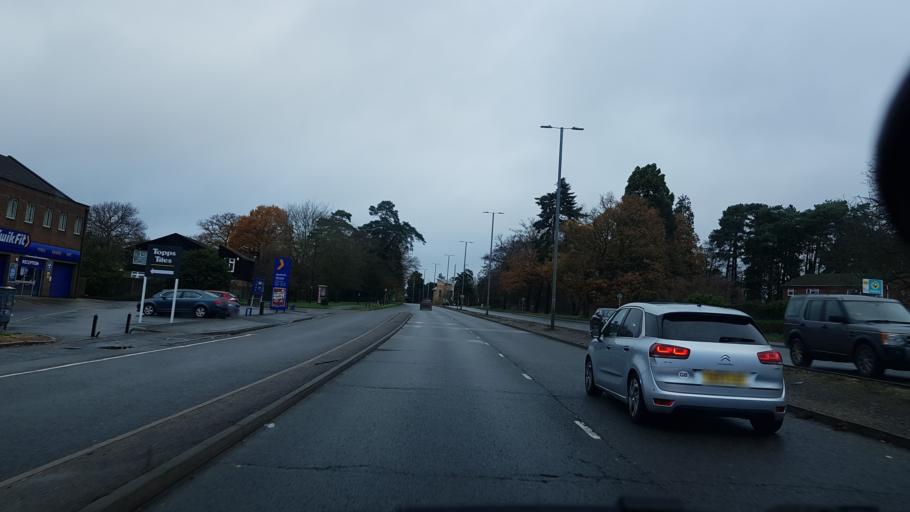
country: GB
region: England
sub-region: Bracknell Forest
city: Bracknell
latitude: 51.4050
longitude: -0.7474
